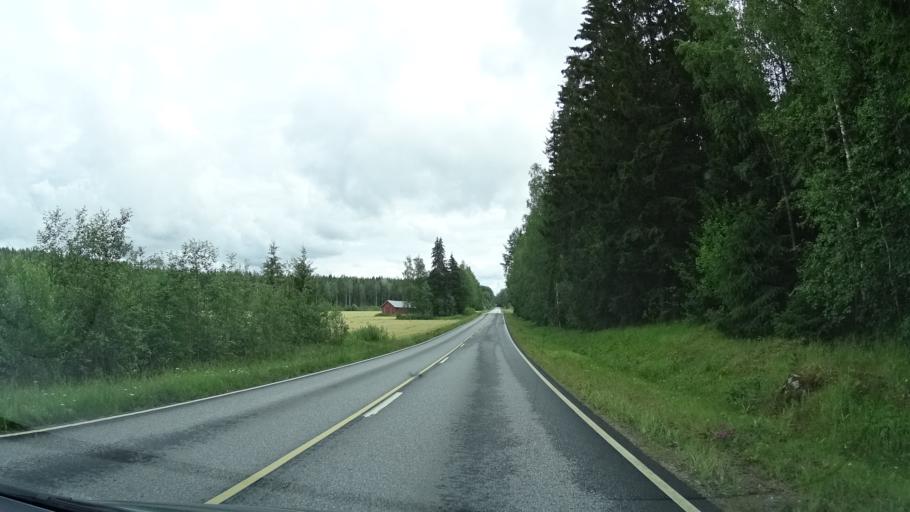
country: FI
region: Haeme
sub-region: Forssa
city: Humppila
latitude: 61.0961
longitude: 23.3579
